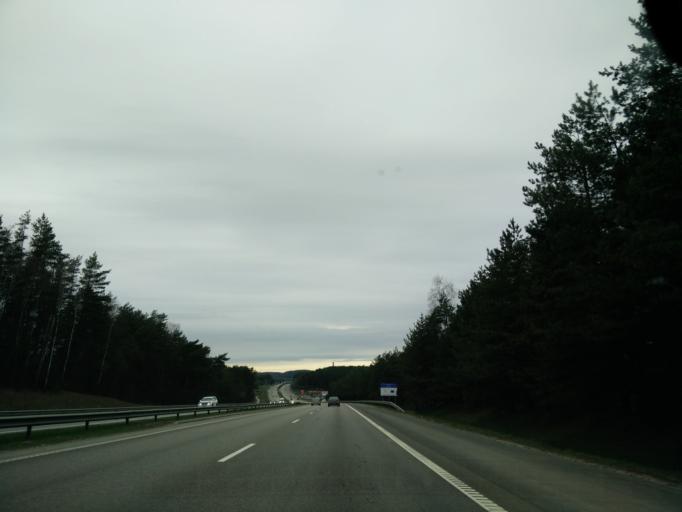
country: LT
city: Grigiskes
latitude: 54.6656
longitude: 25.1201
